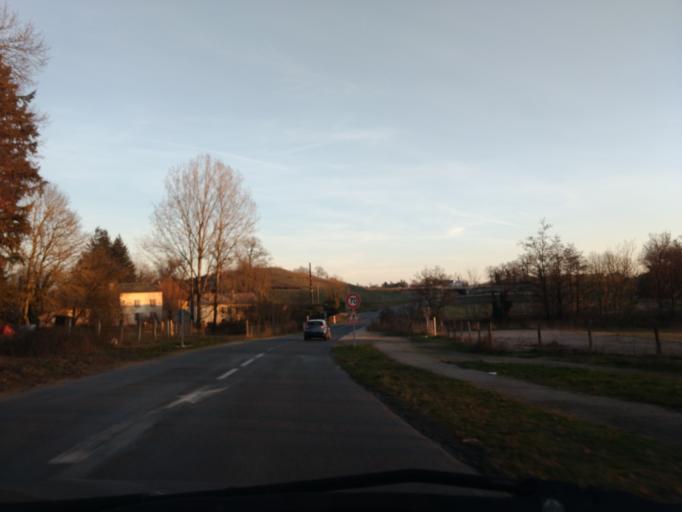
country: FR
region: Midi-Pyrenees
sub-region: Departement de l'Aveyron
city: Naucelle
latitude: 44.1922
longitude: 2.3564
